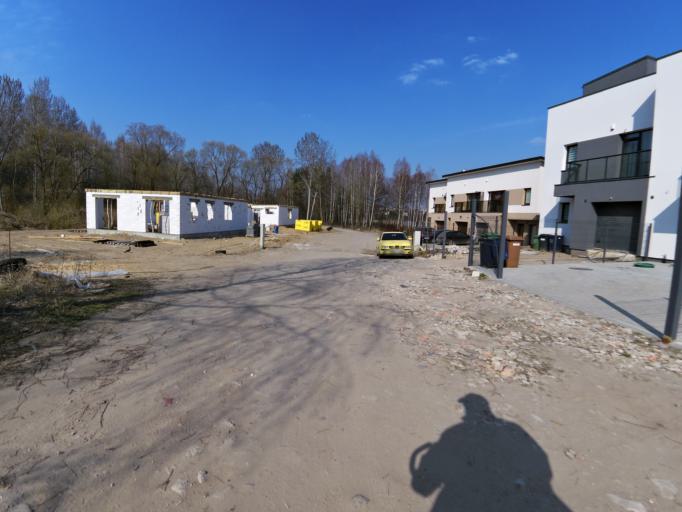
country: LT
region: Vilnius County
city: Pilaite
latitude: 54.6941
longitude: 25.1731
